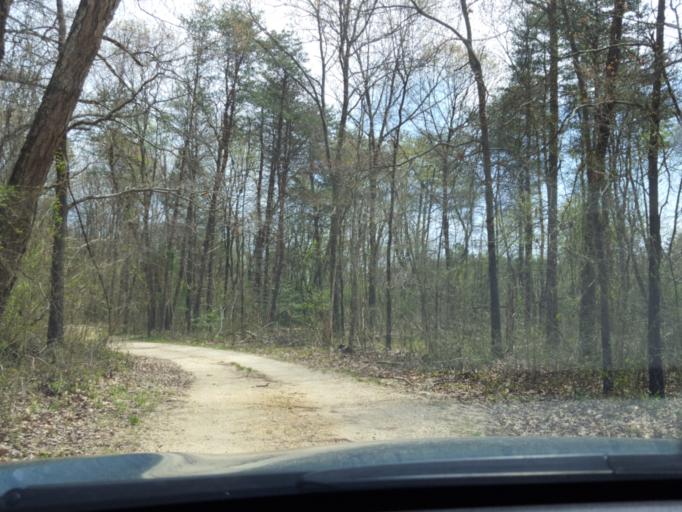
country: US
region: Maryland
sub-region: Calvert County
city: Dunkirk
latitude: 38.7410
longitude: -76.7046
